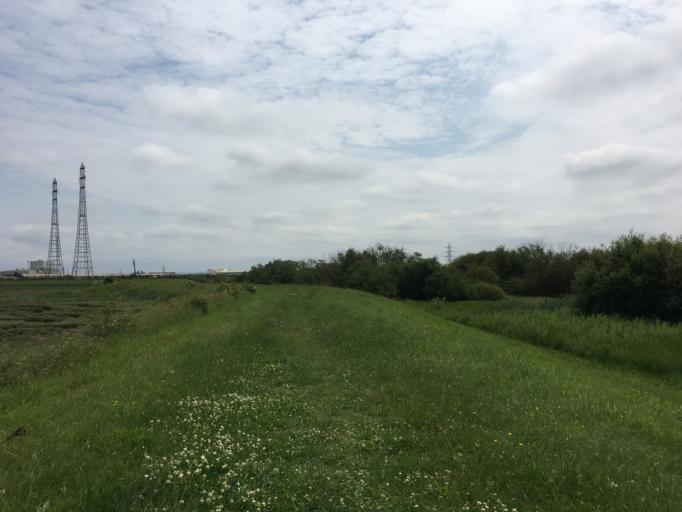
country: GB
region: England
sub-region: Kent
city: Queenborough
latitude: 51.3891
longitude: 0.7492
